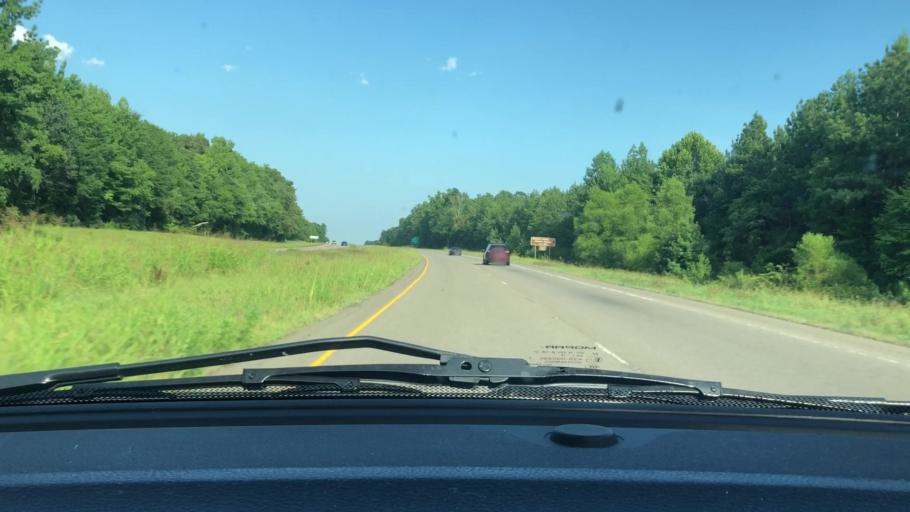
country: US
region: North Carolina
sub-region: Chatham County
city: Farmville
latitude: 35.6103
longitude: -79.3406
